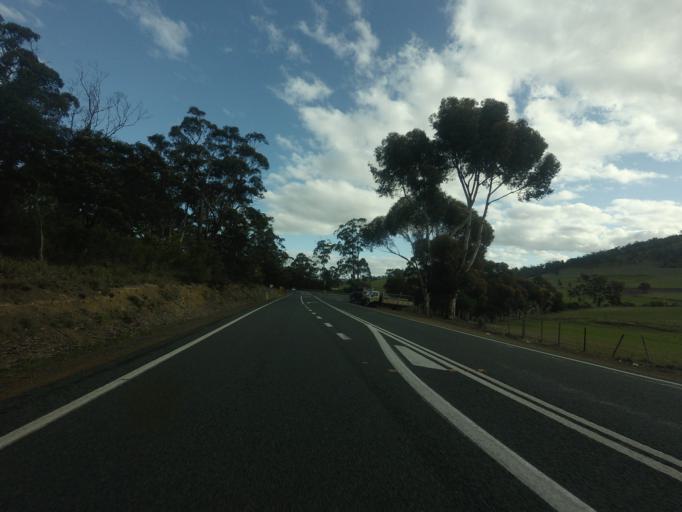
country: AU
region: Tasmania
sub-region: Sorell
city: Sorell
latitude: -42.7076
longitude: 147.5104
